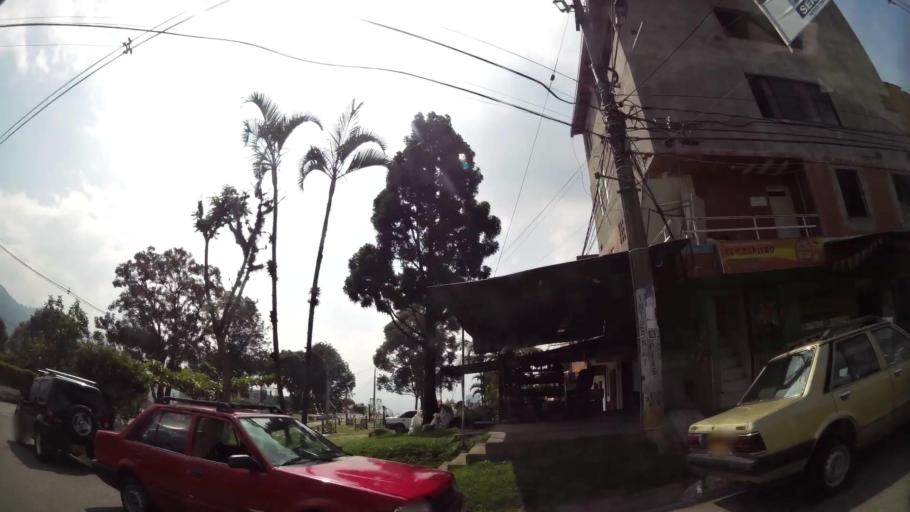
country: CO
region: Antioquia
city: La Estrella
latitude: 6.1801
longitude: -75.6448
